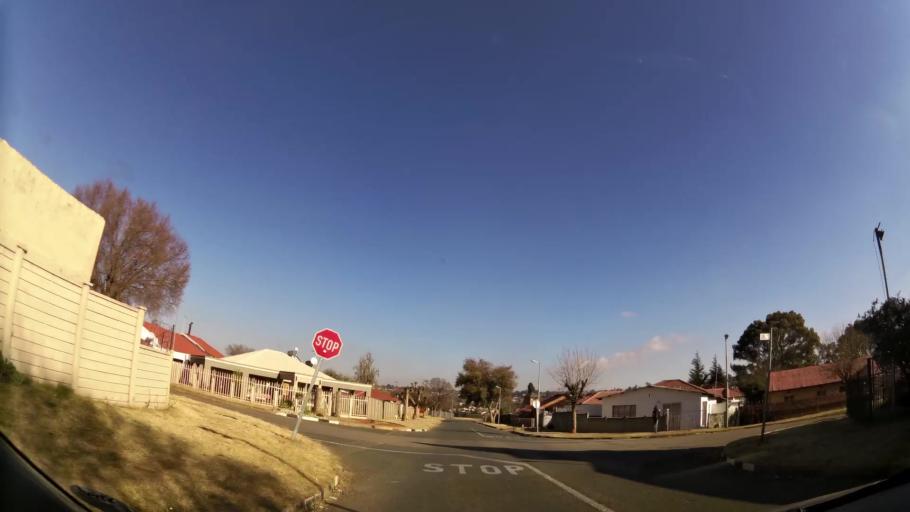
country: ZA
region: Gauteng
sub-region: City of Johannesburg Metropolitan Municipality
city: Roodepoort
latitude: -26.1544
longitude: 27.8508
